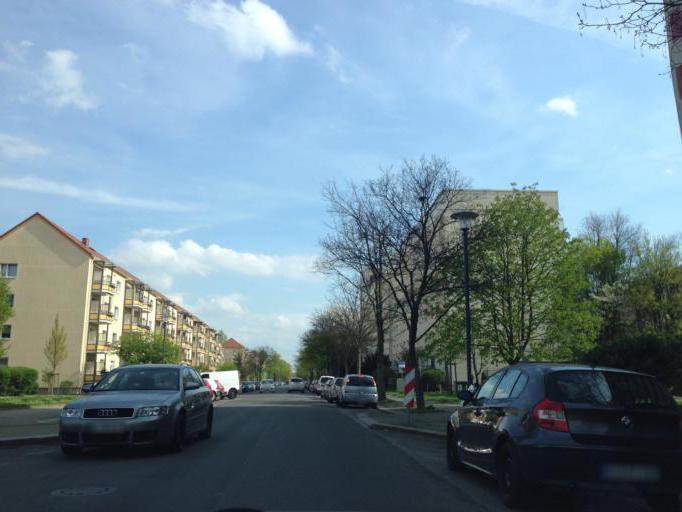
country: DE
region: Saxony
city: Dresden
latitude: 51.0419
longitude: 13.7694
